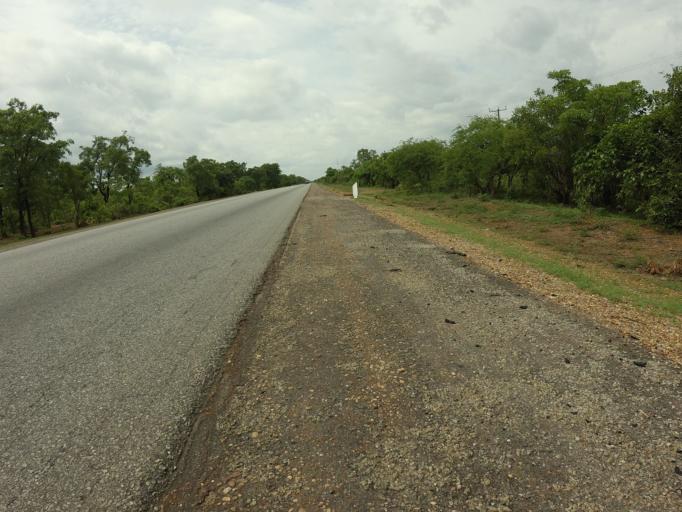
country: GH
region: Brong-Ahafo
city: Kintampo
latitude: 8.6871
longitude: -1.5071
